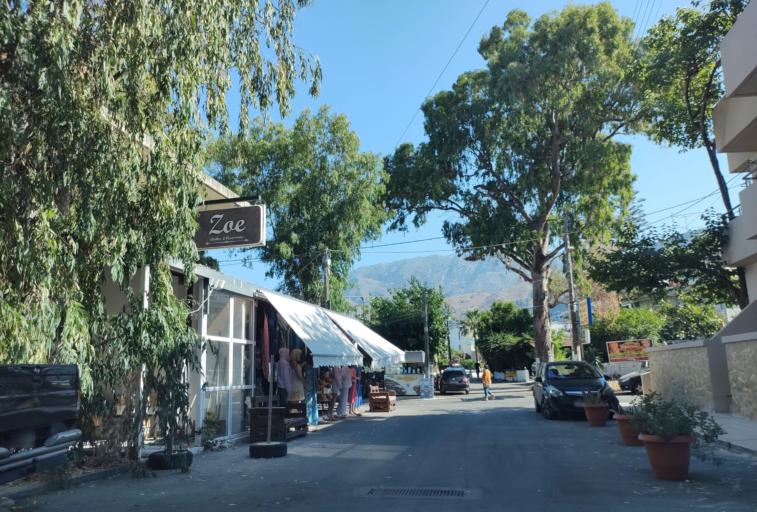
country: GR
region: Crete
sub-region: Nomos Chanias
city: Georgioupolis
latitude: 35.3626
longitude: 24.2606
